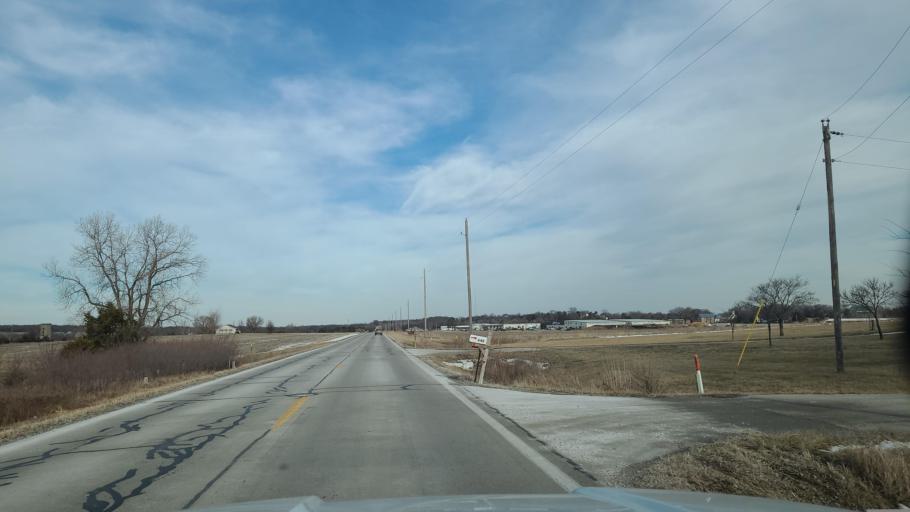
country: US
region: Kansas
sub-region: Douglas County
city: Baldwin City
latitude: 38.8330
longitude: -95.1864
